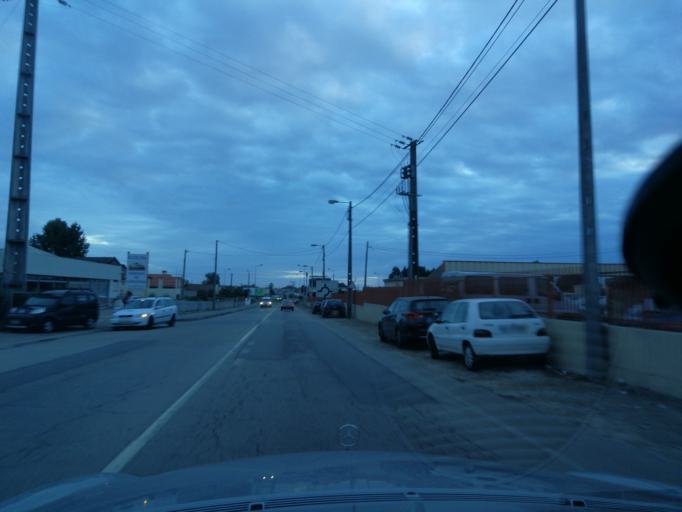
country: PT
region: Aveiro
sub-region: Estarreja
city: Beduido
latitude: 40.7713
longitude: -8.5698
